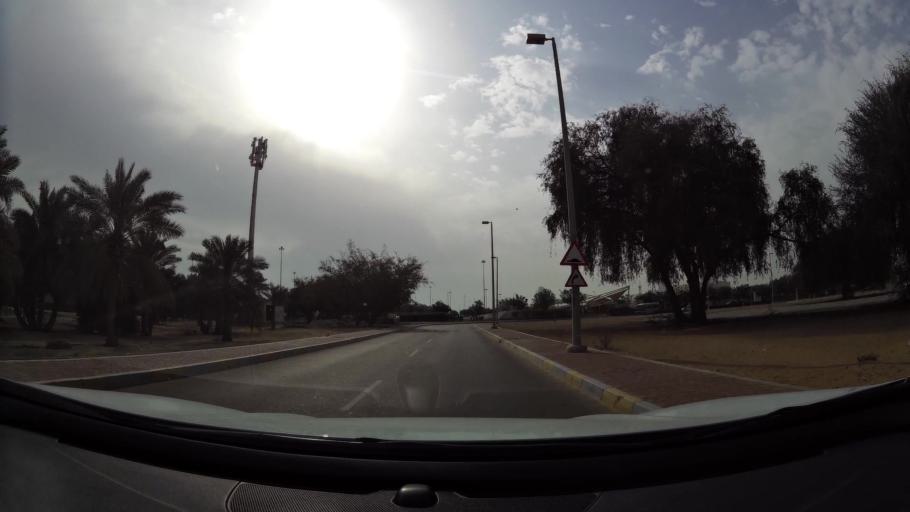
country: AE
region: Abu Dhabi
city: Abu Dhabi
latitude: 24.4742
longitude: 54.3895
